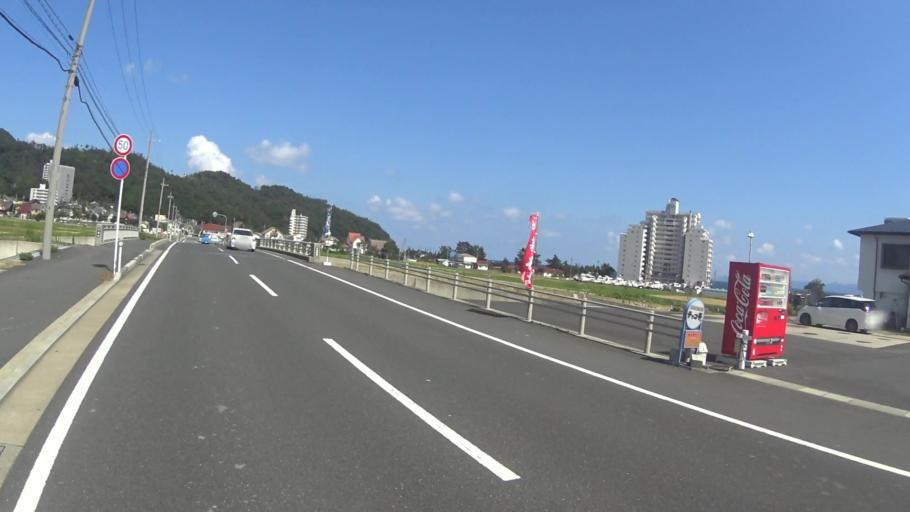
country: JP
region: Kyoto
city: Miyazu
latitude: 35.6123
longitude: 135.2291
